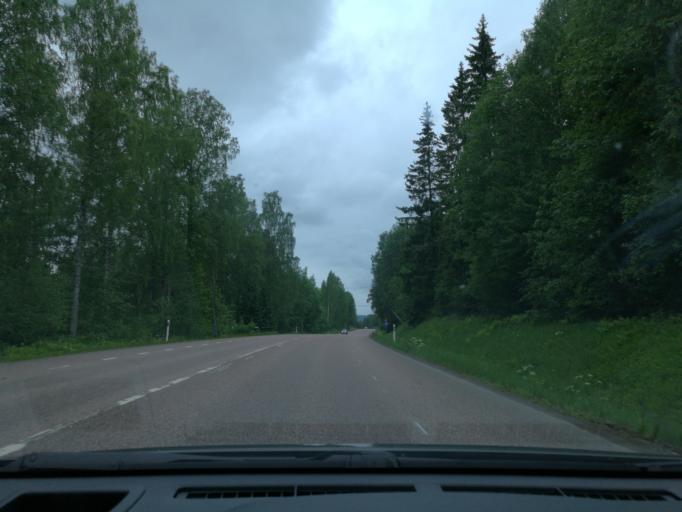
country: SE
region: Dalarna
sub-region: Ludvika Kommun
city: Ludvika
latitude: 60.1460
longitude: 15.2843
